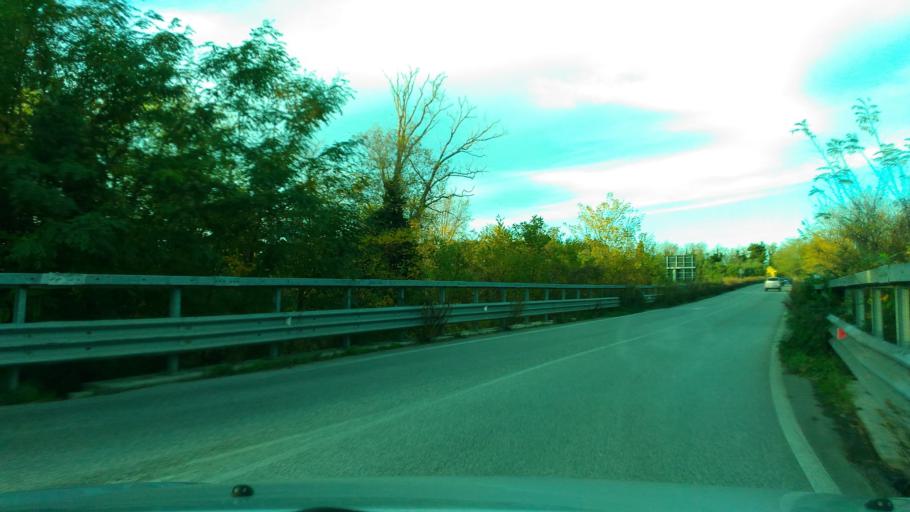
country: IT
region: Tuscany
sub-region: Provincia di Livorno
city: S.P. in Palazzi
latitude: 43.3548
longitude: 10.5072
